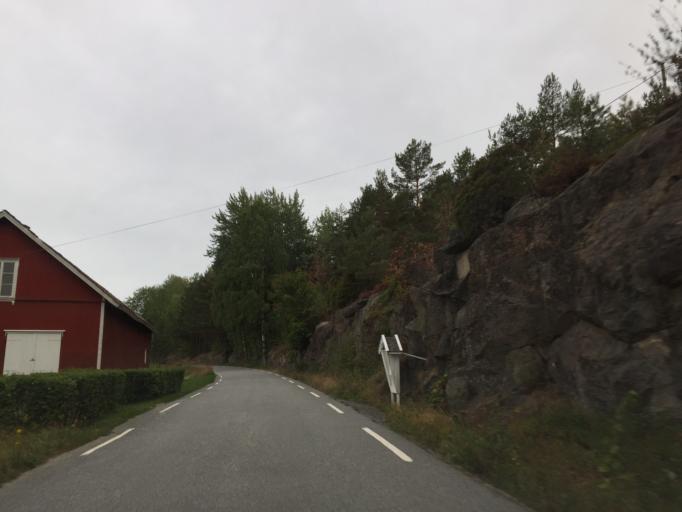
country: NO
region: Ostfold
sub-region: Hvaler
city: Skjaerhalden
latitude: 59.0685
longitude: 11.0053
